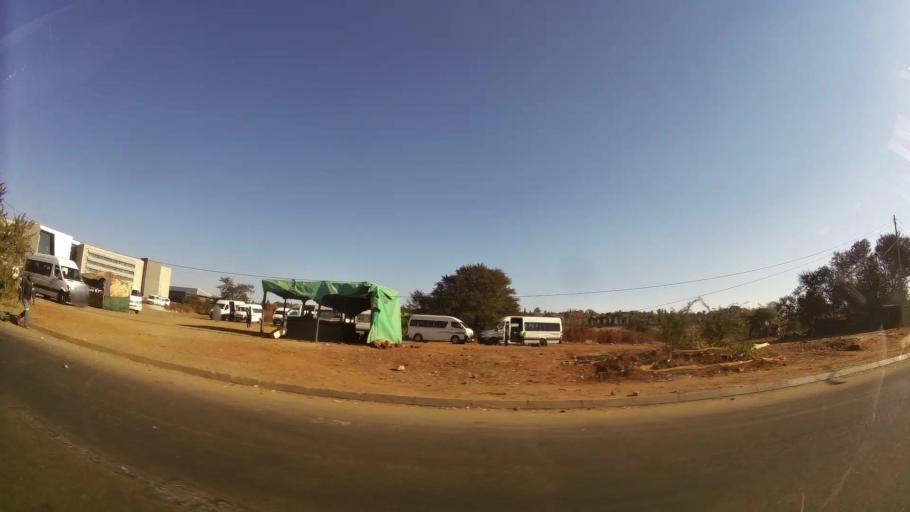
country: ZA
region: Gauteng
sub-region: City of Tshwane Metropolitan Municipality
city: Centurion
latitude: -25.8584
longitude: 28.1843
